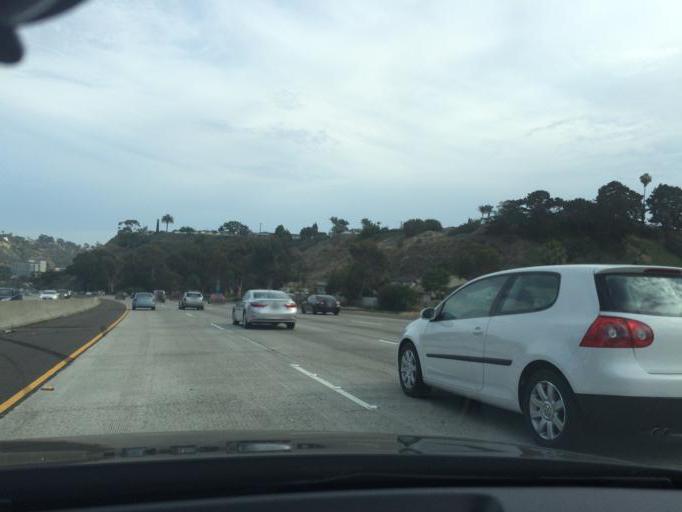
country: US
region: California
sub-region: San Diego County
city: San Diego
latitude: 32.7793
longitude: -117.1631
